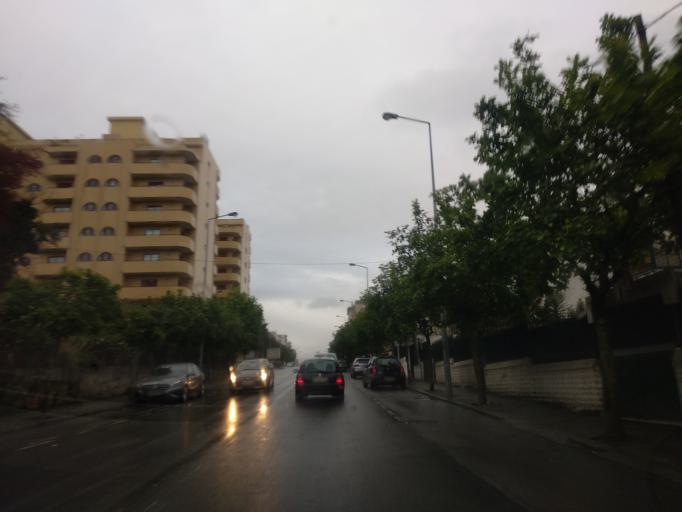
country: PT
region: Porto
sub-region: Gondomar
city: Rio Tinto
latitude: 41.1754
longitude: -8.5573
